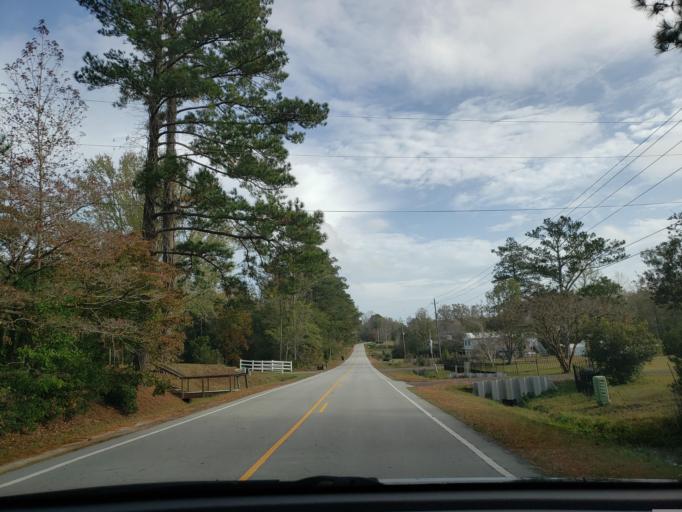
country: US
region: North Carolina
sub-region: Onslow County
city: Jacksonville
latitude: 34.6694
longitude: -77.4960
